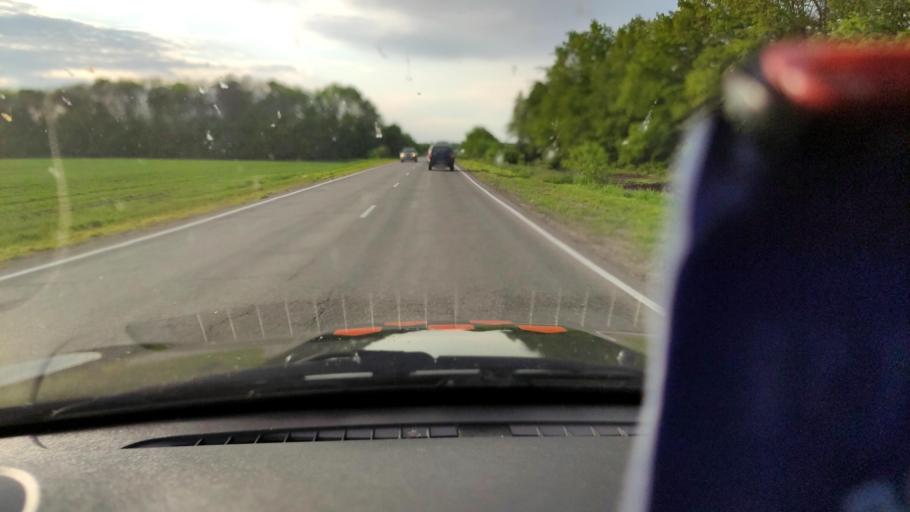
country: RU
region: Voronezj
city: Shilovo
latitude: 51.4404
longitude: 38.9973
